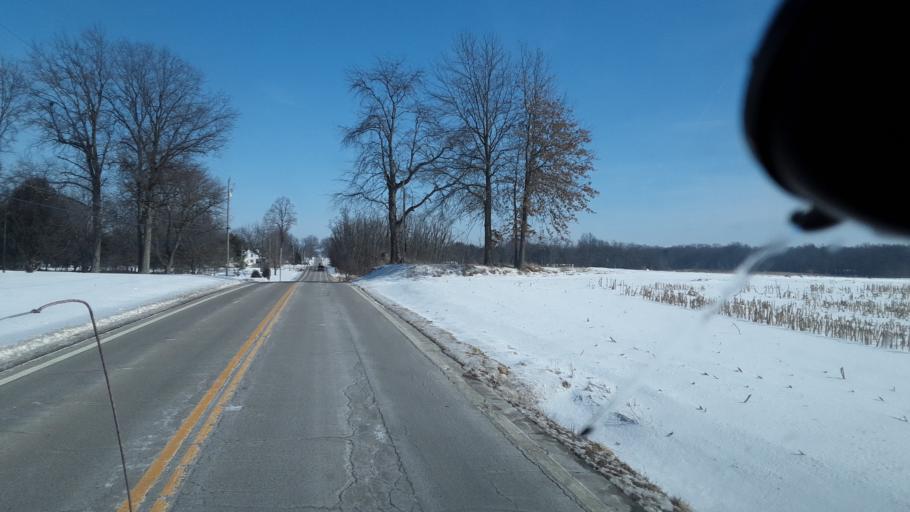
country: US
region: Ohio
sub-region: Columbiana County
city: Salem
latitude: 40.9449
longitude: -80.9118
